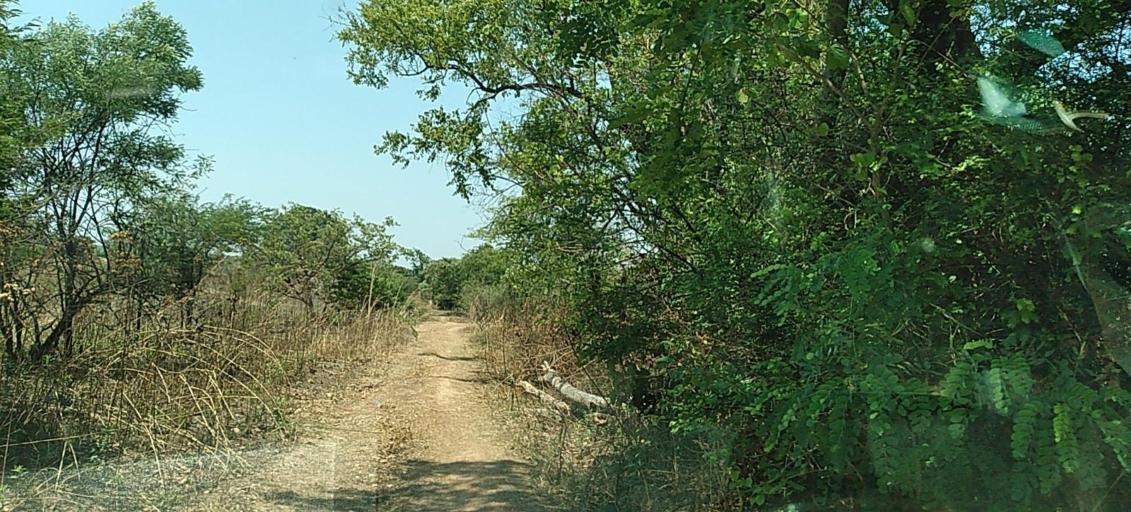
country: ZM
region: Copperbelt
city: Luanshya
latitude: -12.9906
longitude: 28.3255
